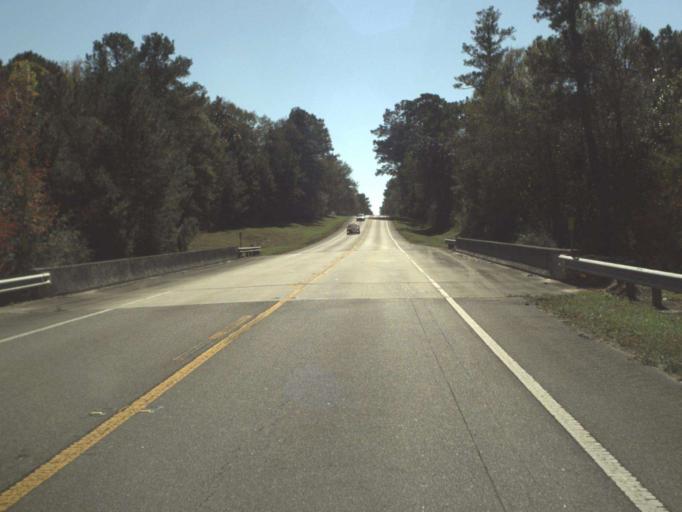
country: US
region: Florida
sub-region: Okaloosa County
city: Crestview
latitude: 30.9738
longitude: -86.6310
